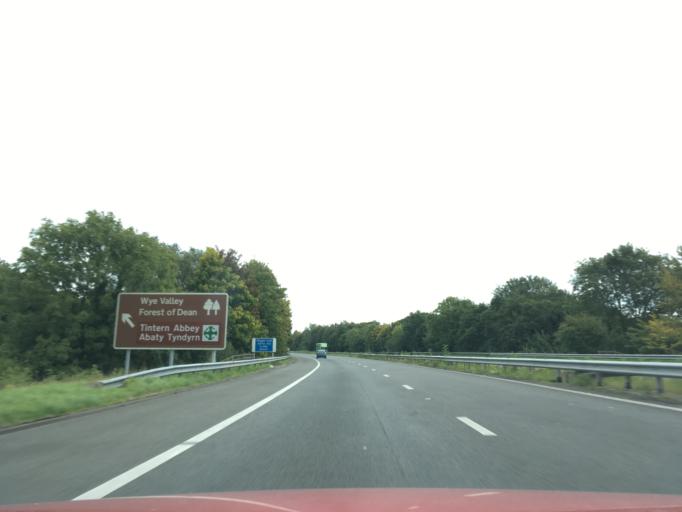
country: GB
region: Wales
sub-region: Monmouthshire
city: Chepstow
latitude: 51.6167
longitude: -2.6988
